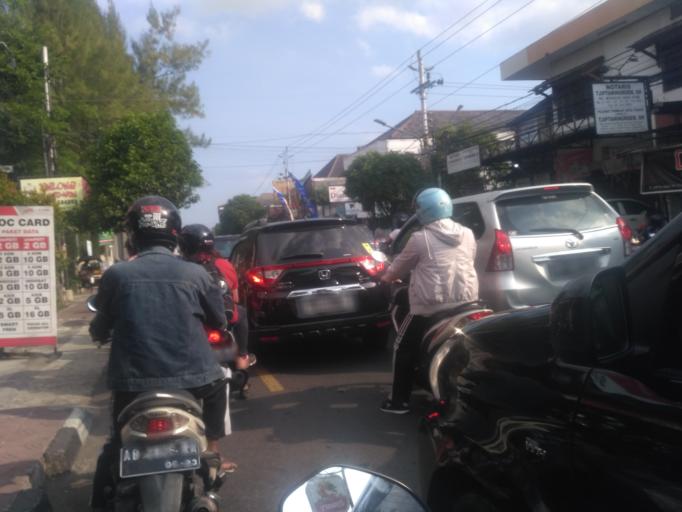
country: ID
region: Daerah Istimewa Yogyakarta
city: Yogyakarta
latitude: -7.7808
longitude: 110.3674
